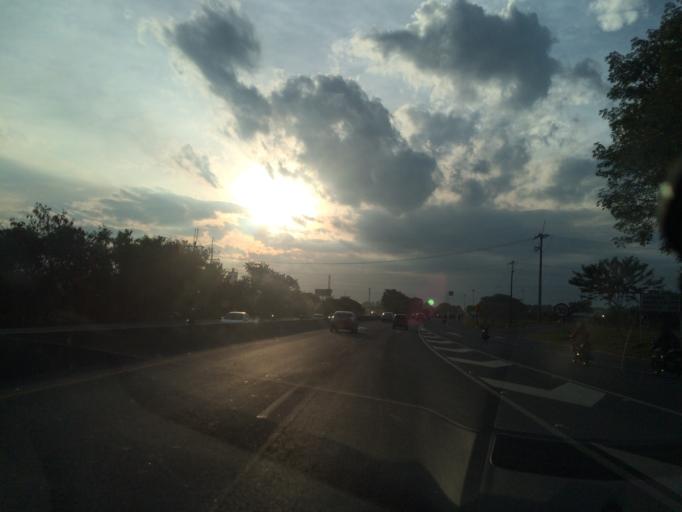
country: CO
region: Valle del Cauca
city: Cali
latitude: 3.4929
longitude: -76.4823
